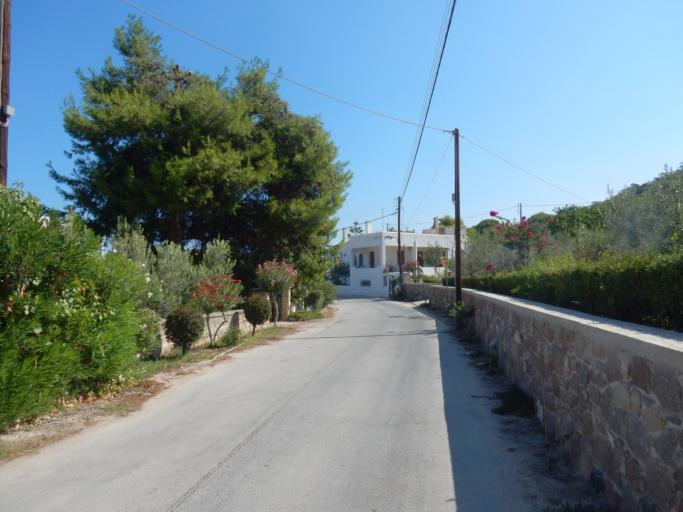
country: GR
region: Attica
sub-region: Nomos Piraios
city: Vathi
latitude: 37.7683
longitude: 23.5366
